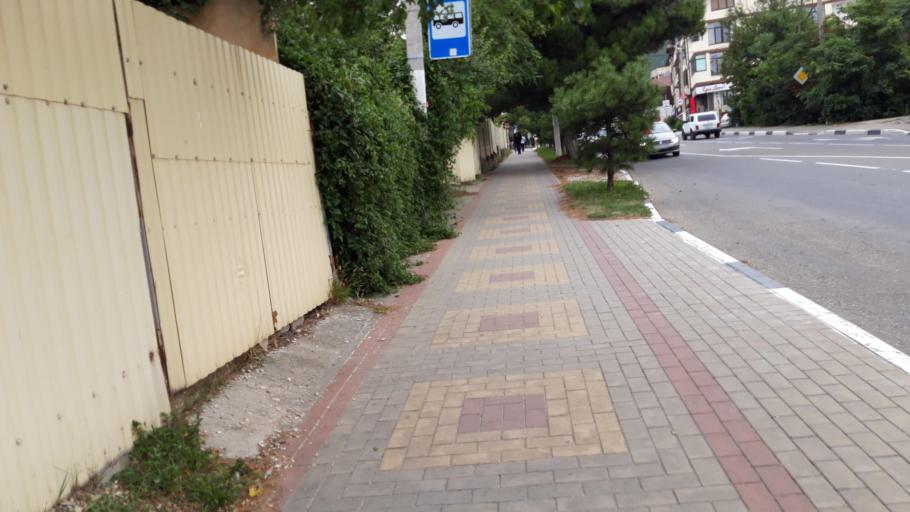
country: RU
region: Krasnodarskiy
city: Gelendzhik
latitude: 44.5660
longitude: 38.0877
